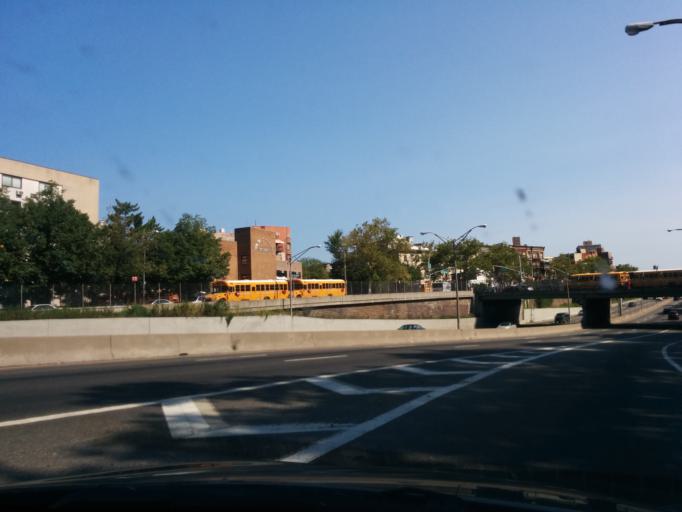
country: US
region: New York
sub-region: Queens County
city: Long Island City
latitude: 40.7021
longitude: -73.9604
